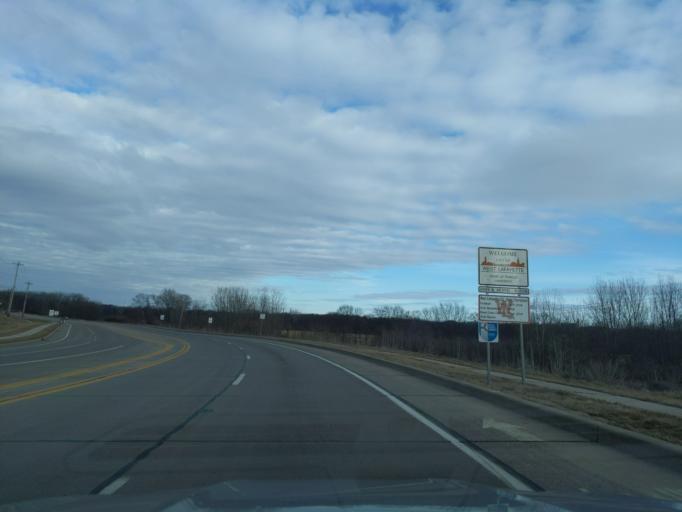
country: US
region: Indiana
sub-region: Tippecanoe County
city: West Lafayette
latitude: 40.4082
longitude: -86.9183
